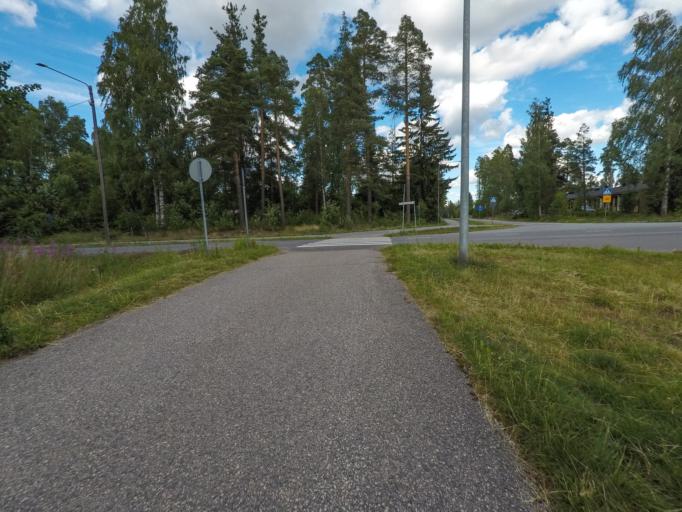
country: FI
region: South Karelia
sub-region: Lappeenranta
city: Joutseno
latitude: 61.1211
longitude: 28.4748
